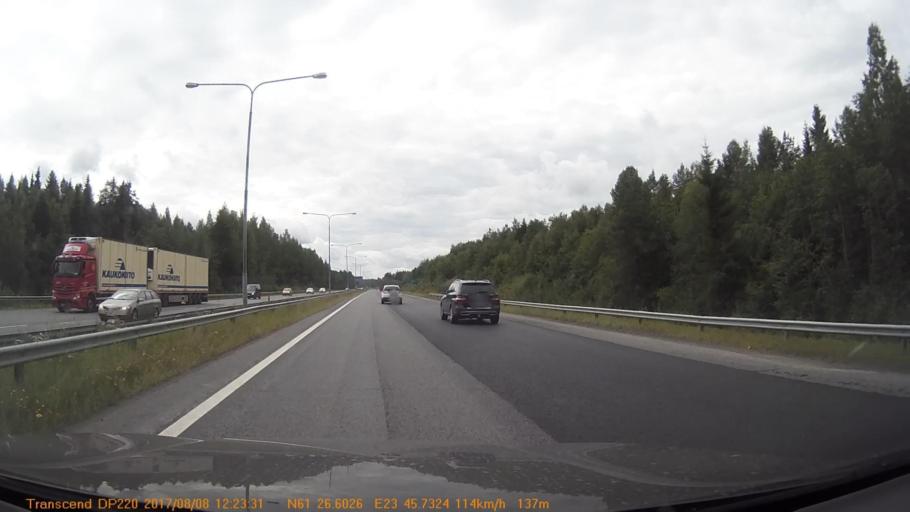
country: FI
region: Pirkanmaa
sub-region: Tampere
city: Tampere
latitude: 61.4429
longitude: 23.7619
